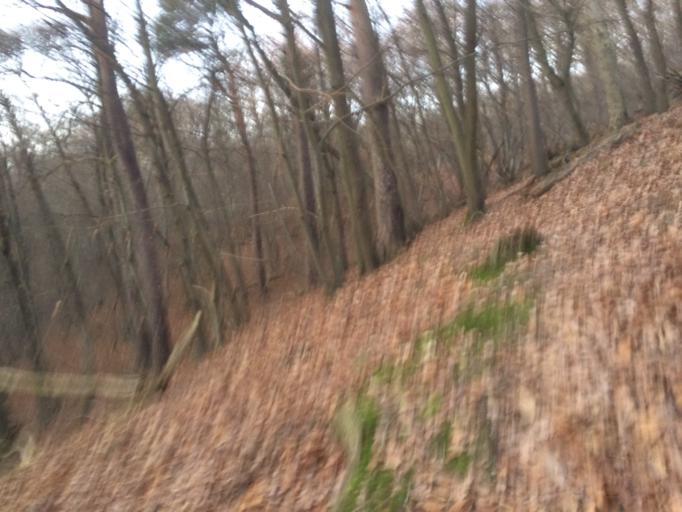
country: FR
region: Ile-de-France
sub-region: Departement de l'Essonne
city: Verrieres-le-Buisson
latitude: 48.7512
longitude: 2.2527
